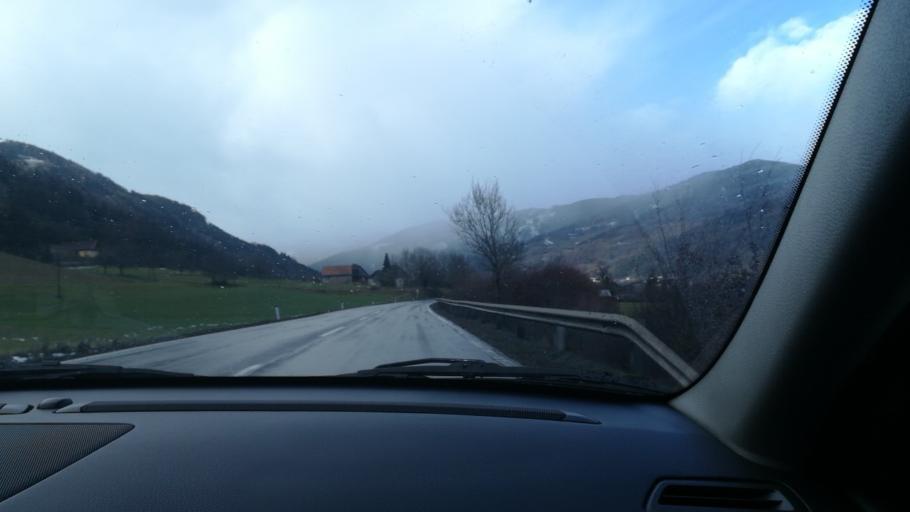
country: AT
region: Styria
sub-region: Politischer Bezirk Murtal
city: Sankt Georgen ob Judenburg
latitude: 47.2015
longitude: 14.5150
